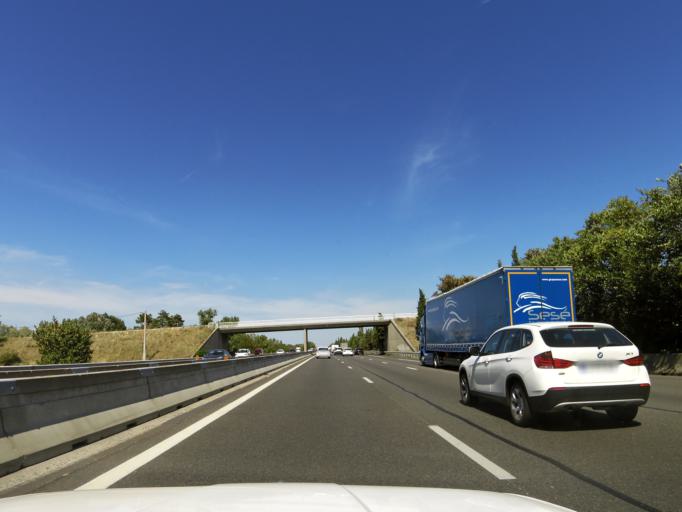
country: FR
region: Rhone-Alpes
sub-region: Departement de la Drome
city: Etoile-sur-Rhone
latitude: 44.8273
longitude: 4.8604
